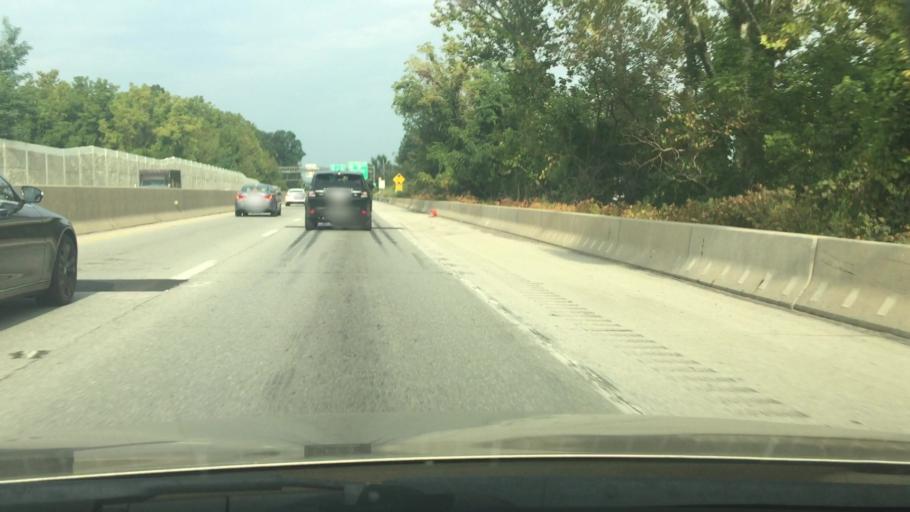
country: US
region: Pennsylvania
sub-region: Montgomery County
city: King of Prussia
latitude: 40.0782
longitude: -75.3734
